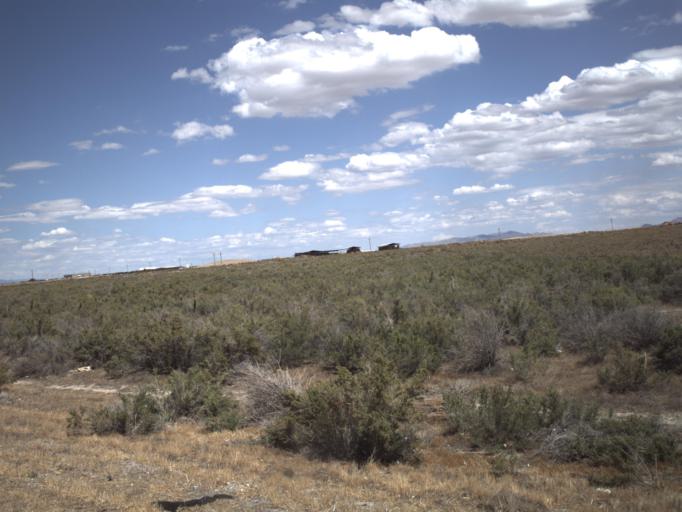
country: US
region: Utah
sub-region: Millard County
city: Delta
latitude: 39.3147
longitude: -112.4789
